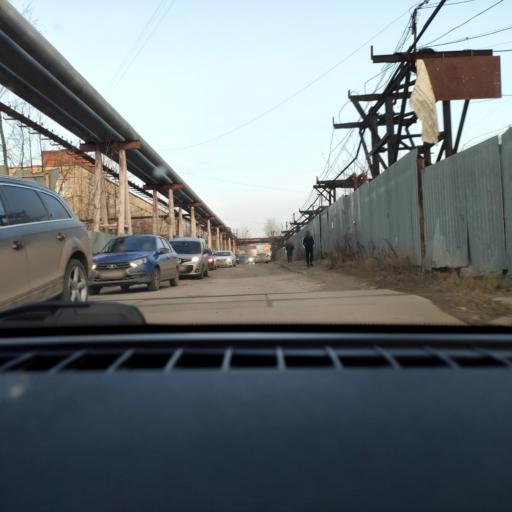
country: RU
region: Perm
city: Froly
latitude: 57.9617
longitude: 56.2728
